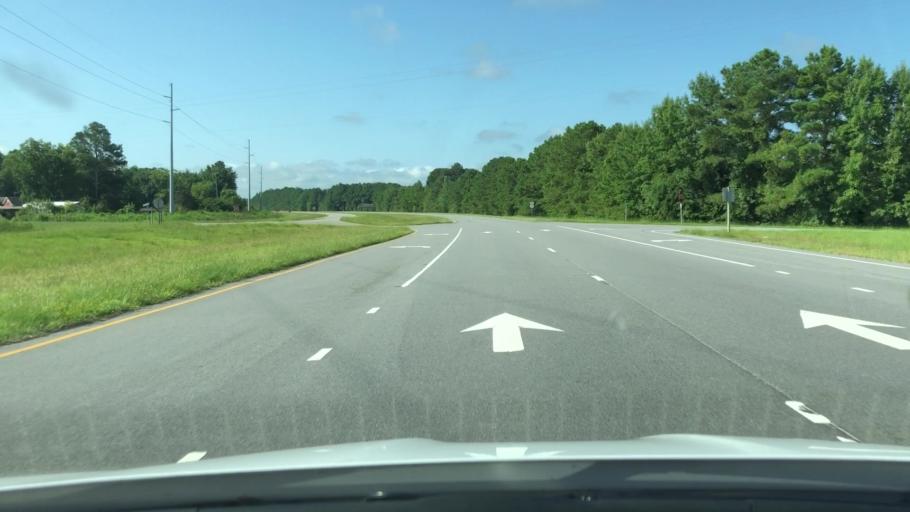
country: US
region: North Carolina
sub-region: Pasquotank County
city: Elizabeth City
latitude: 36.4470
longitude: -76.3381
